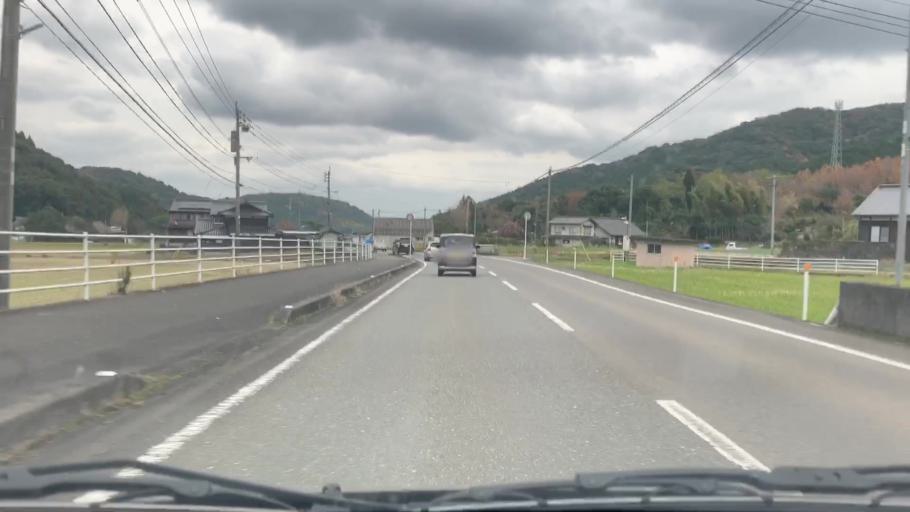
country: JP
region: Saga Prefecture
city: Kashima
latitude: 33.0988
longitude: 130.0528
